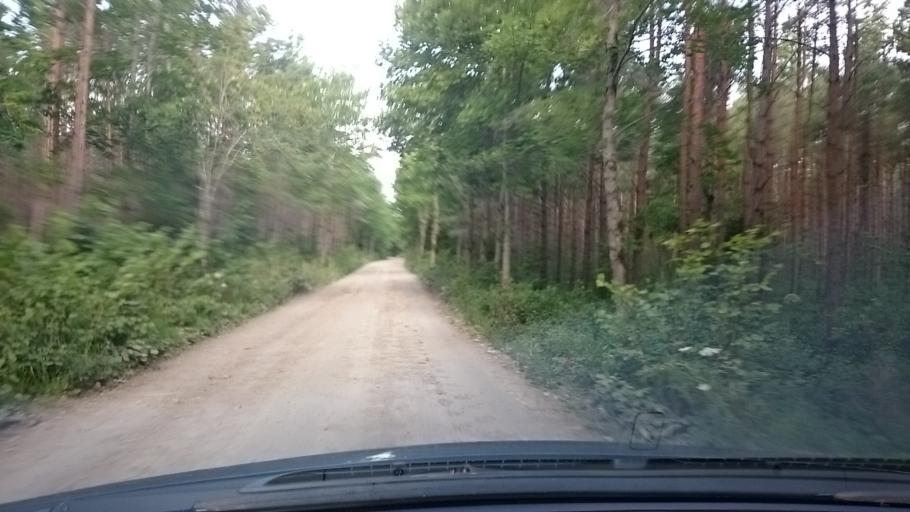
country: EE
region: Saare
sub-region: Kuressaare linn
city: Kuressaare
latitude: 58.3271
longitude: 21.9752
